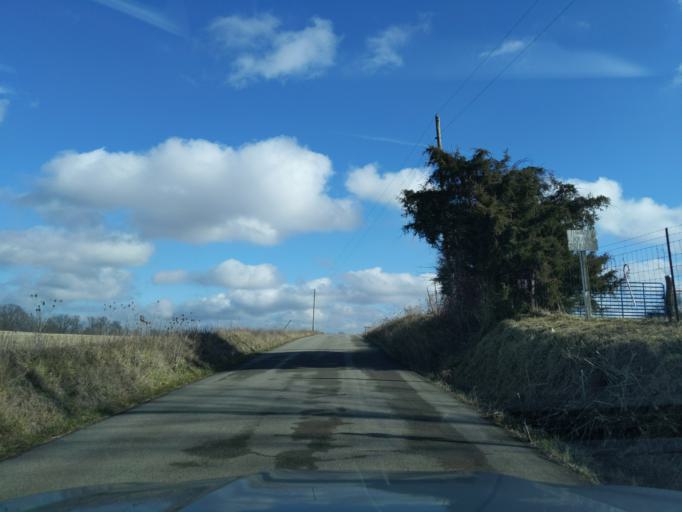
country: US
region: Indiana
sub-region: Decatur County
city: Greensburg
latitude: 39.2782
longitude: -85.4495
